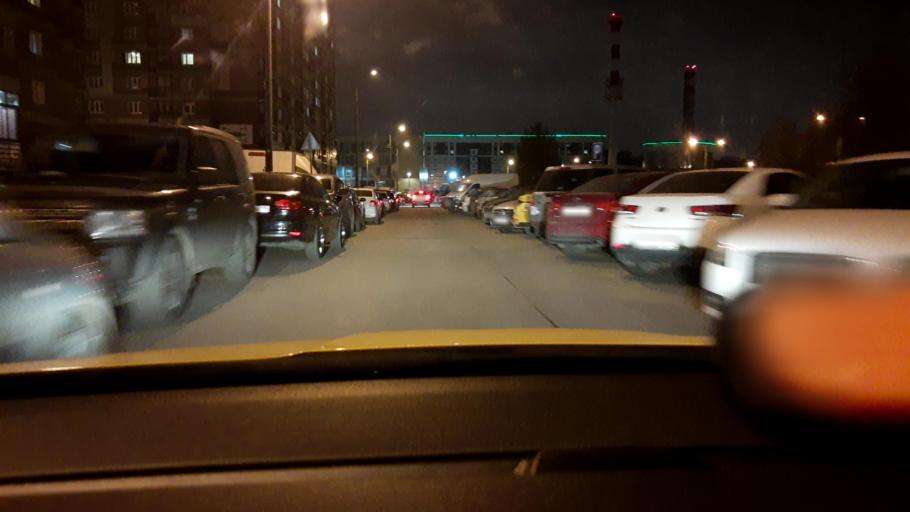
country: RU
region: Moscow
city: Khimki
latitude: 55.8704
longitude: 37.4033
